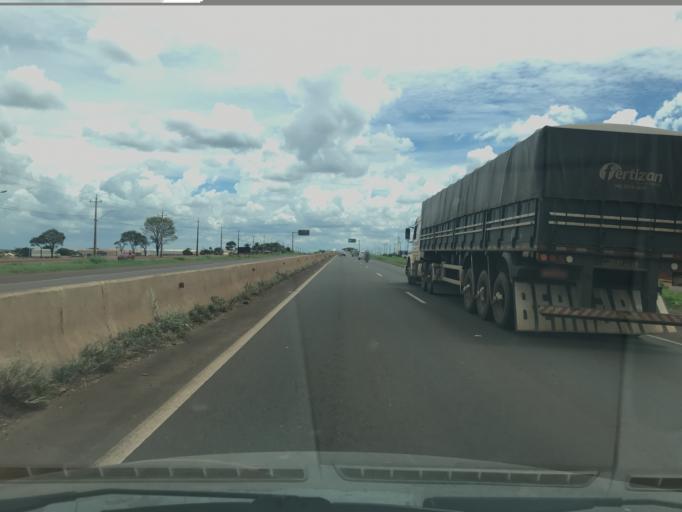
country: BR
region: Parana
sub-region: Paicandu
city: Paicandu
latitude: -23.4556
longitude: -52.0169
